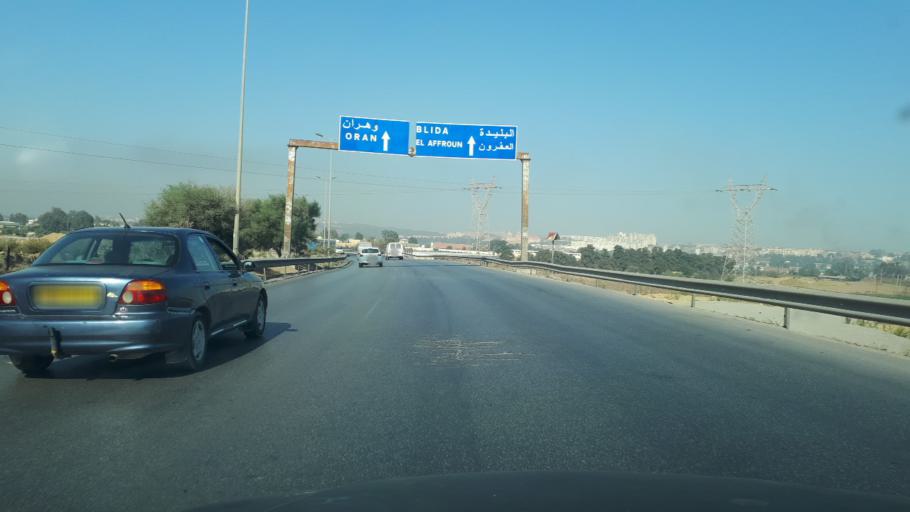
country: DZ
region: Tipaza
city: Baraki
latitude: 36.6830
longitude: 3.0992
